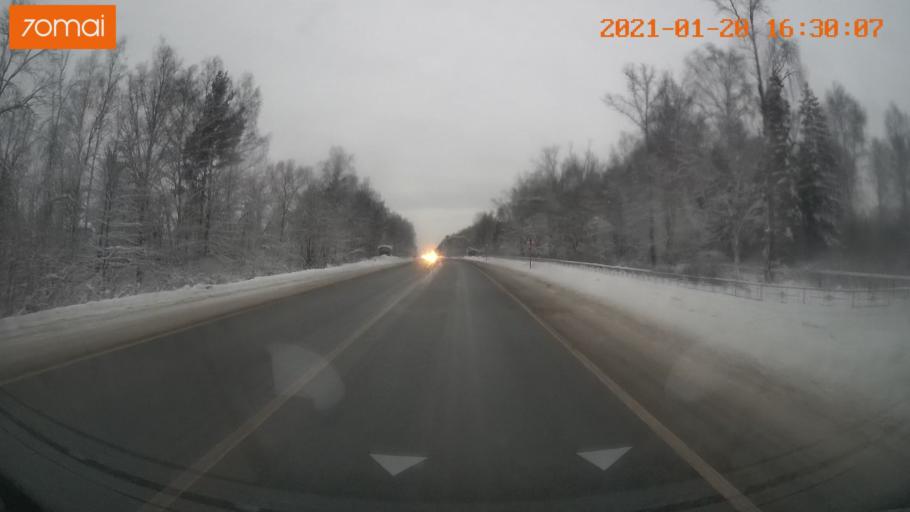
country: RU
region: Vladimir
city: Kameshkovo
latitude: 56.1964
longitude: 40.8780
